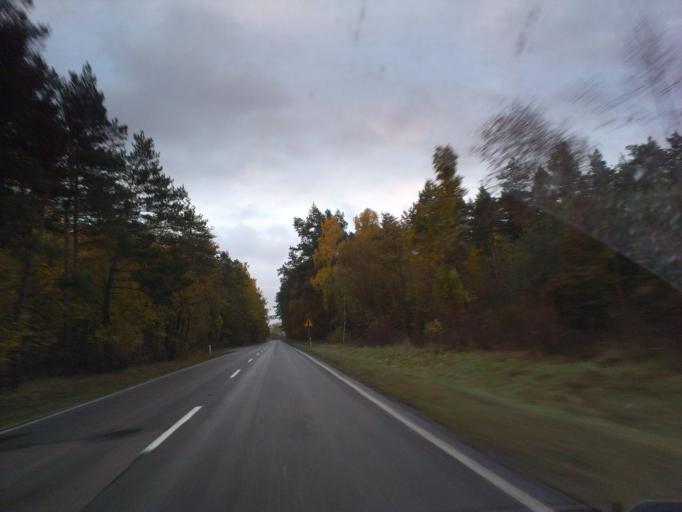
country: PL
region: Kujawsko-Pomorskie
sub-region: Powiat tucholski
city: Cekcyn
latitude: 53.5240
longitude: 17.9495
